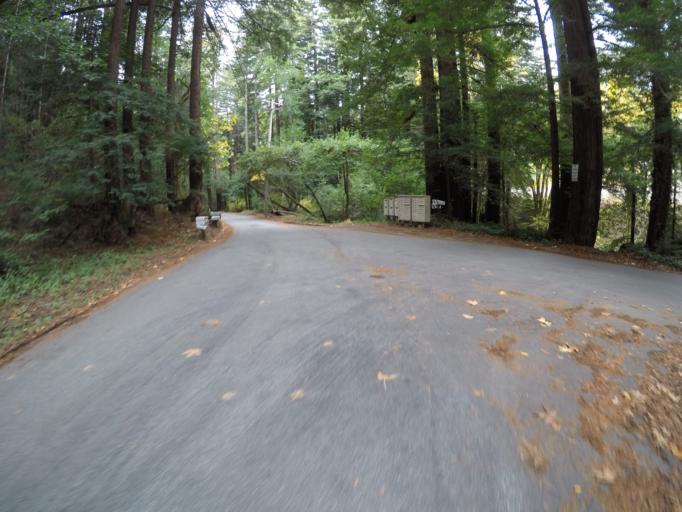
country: US
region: California
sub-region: Santa Cruz County
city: Scotts Valley
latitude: 37.0394
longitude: -121.9764
